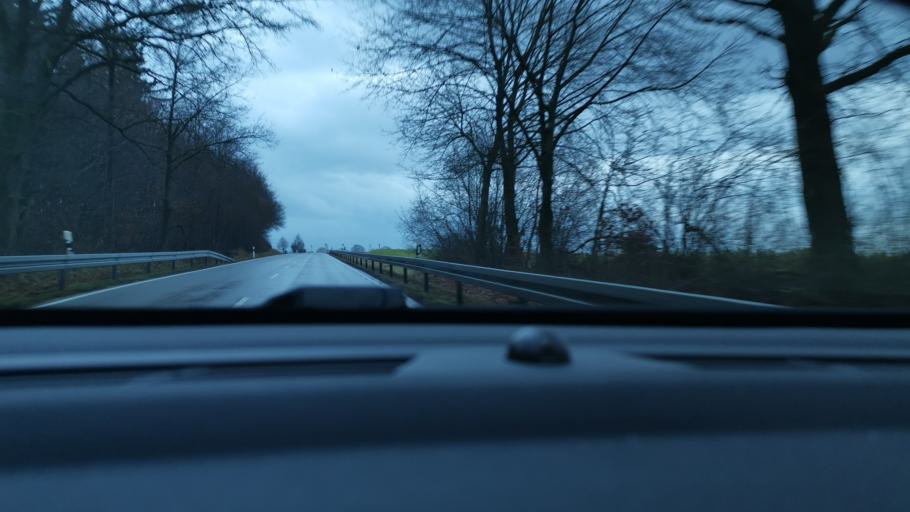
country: DE
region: Bavaria
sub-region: Swabia
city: Petersdorf
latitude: 48.5287
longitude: 11.0283
